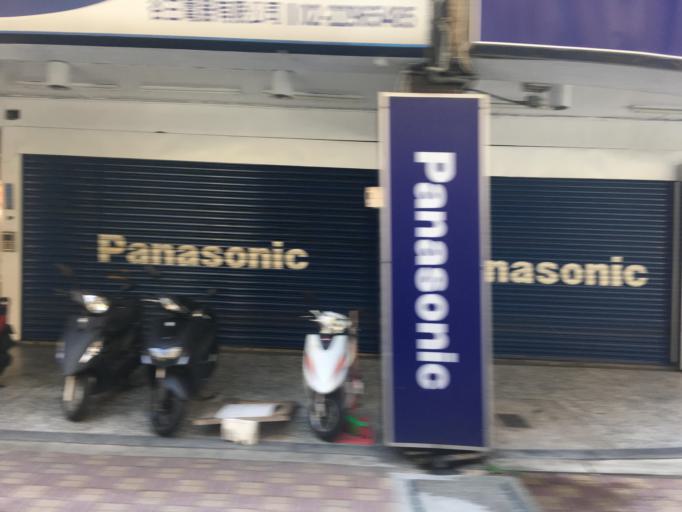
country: TW
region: Taipei
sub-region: Taipei
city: Banqiao
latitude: 25.0495
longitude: 121.4274
